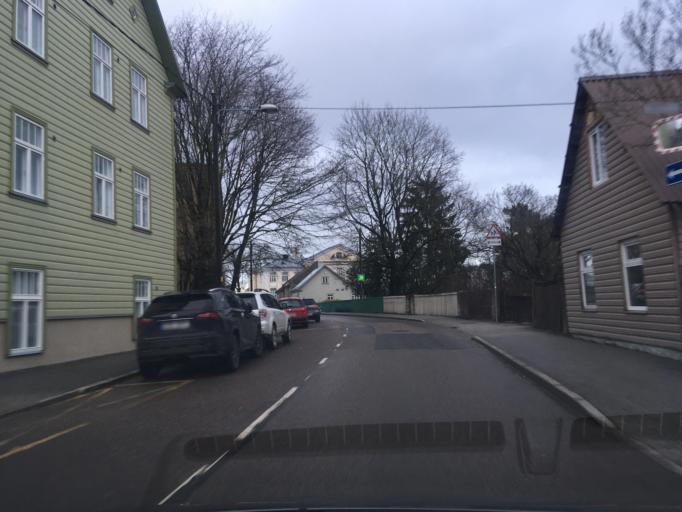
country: EE
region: Tartu
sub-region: Tartu linn
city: Tartu
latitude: 58.3700
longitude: 26.7343
